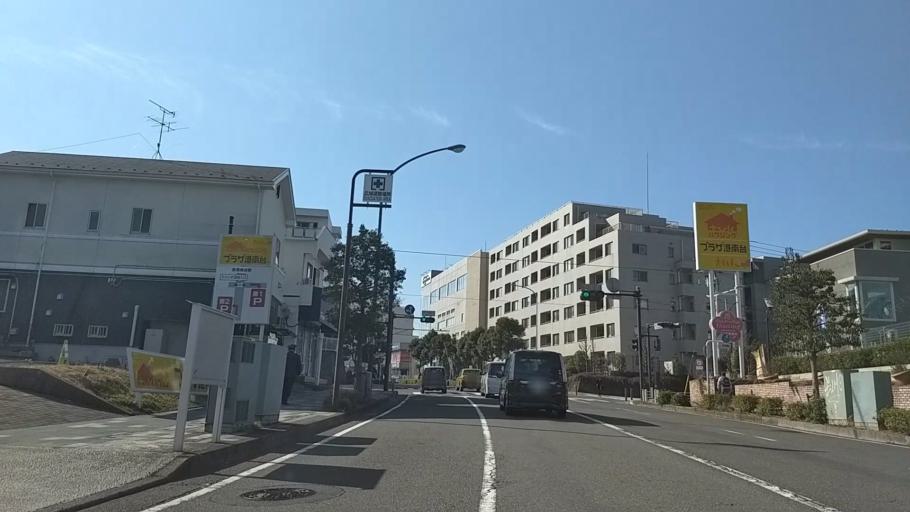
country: JP
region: Kanagawa
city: Kamakura
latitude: 35.3778
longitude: 139.5759
